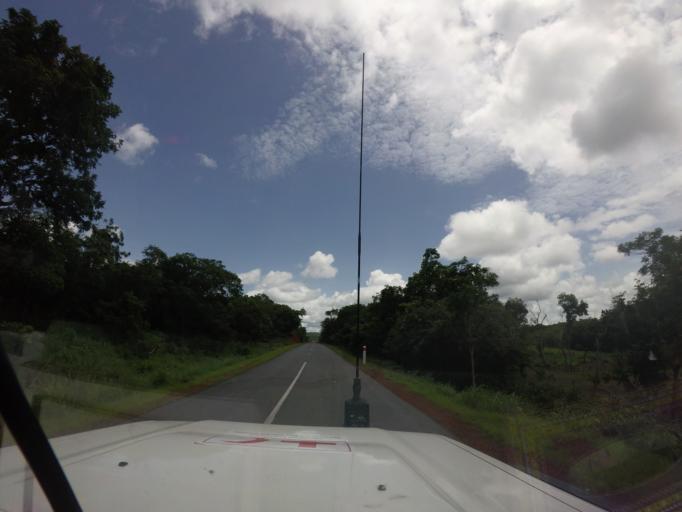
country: SL
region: Northern Province
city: Gberia Fotombu
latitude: 10.0901
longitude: -11.1283
